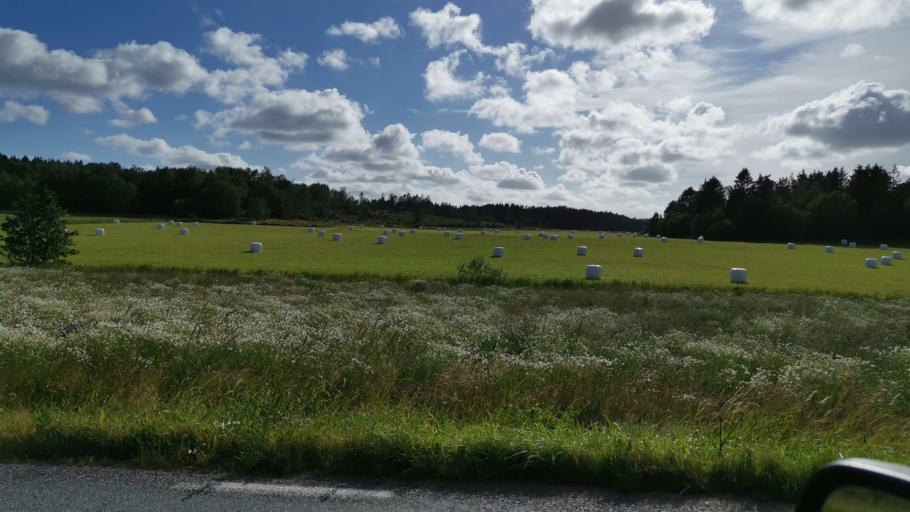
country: SE
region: Vaestra Goetaland
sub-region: Orust
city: Henan
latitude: 58.1662
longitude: 11.6018
